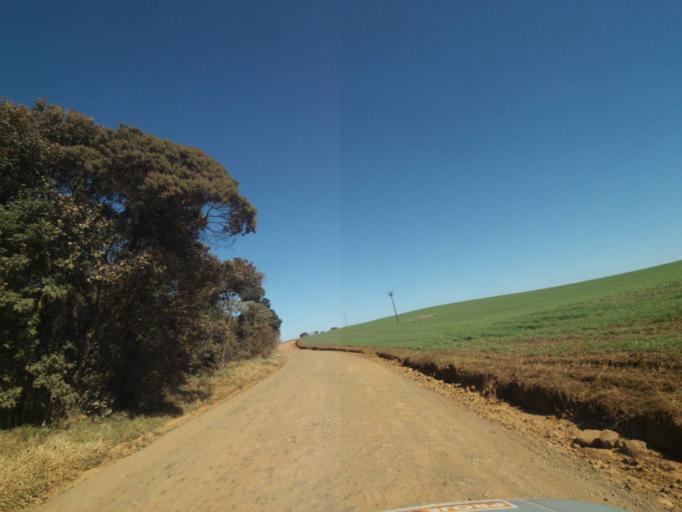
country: BR
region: Parana
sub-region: Tibagi
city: Tibagi
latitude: -24.6160
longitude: -50.6070
